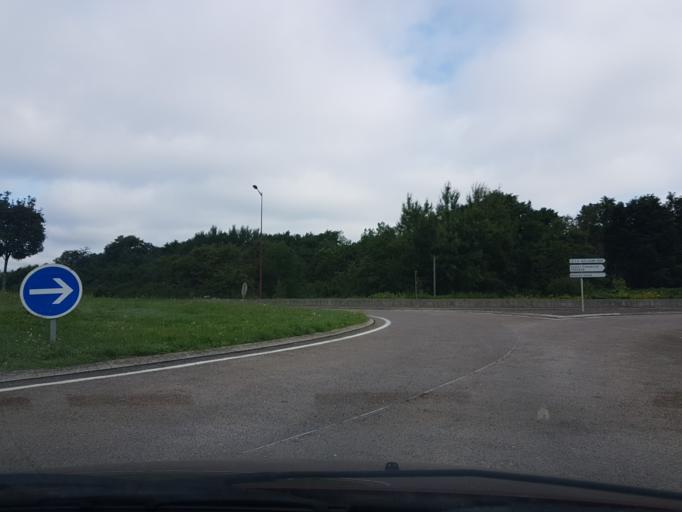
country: FR
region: Franche-Comte
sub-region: Departement de la Haute-Saone
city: Luxeuil-les-Bains
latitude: 47.8068
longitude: 6.3679
